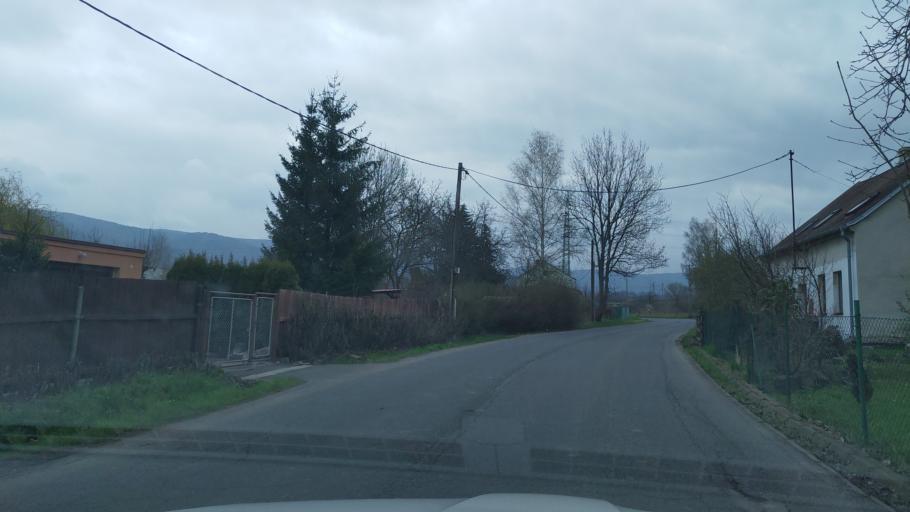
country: CZ
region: Ustecky
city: Chabarovice
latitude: 50.6797
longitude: 13.9400
